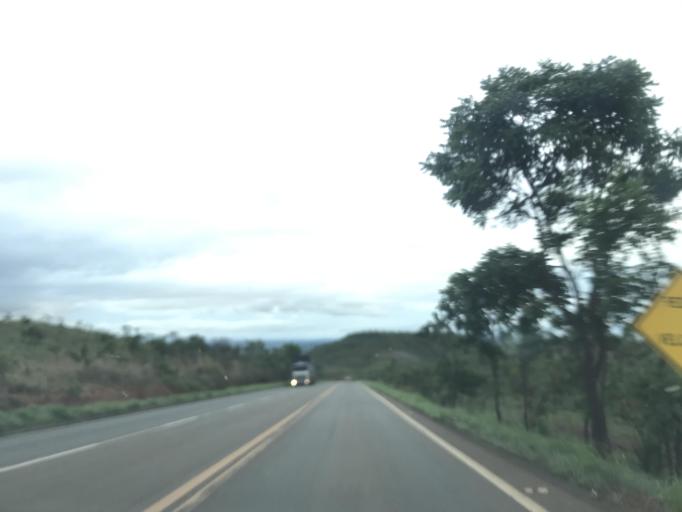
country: BR
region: Goias
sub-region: Luziania
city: Luziania
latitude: -16.4007
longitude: -48.1108
